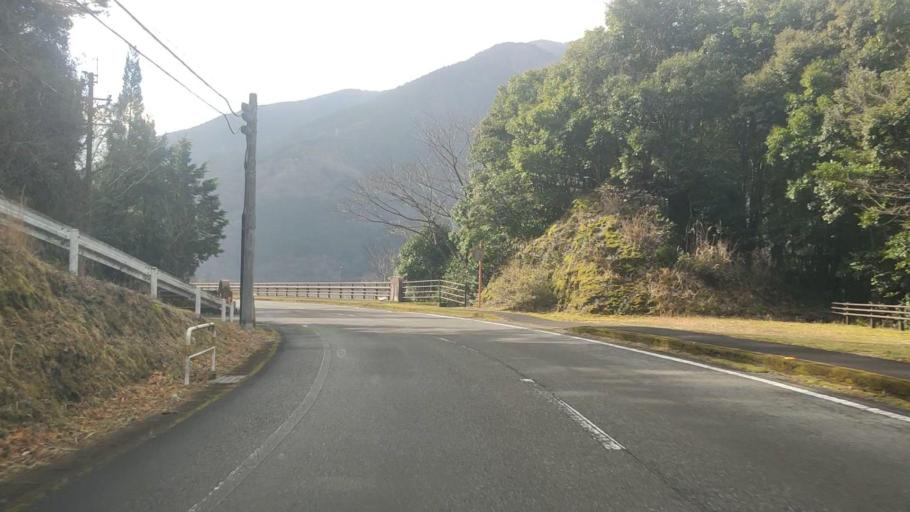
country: JP
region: Kumamoto
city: Hitoyoshi
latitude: 32.4040
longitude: 130.8258
